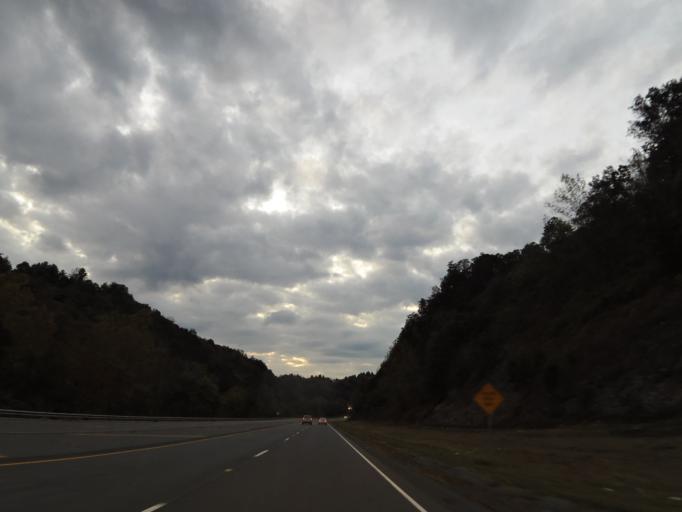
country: US
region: North Carolina
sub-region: Madison County
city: Marshall
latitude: 35.7697
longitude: -82.6202
